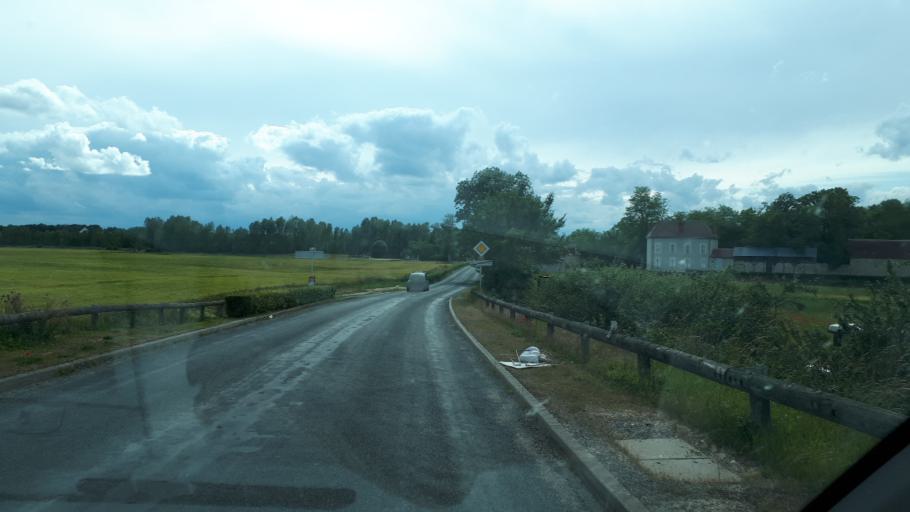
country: FR
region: Centre
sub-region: Departement du Cher
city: Mehun-sur-Yevre
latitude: 47.0800
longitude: 2.1946
